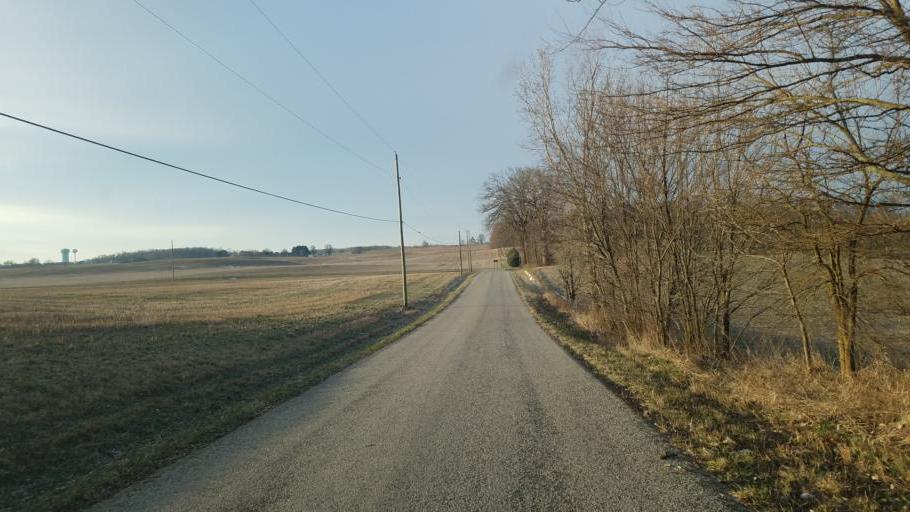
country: US
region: Ohio
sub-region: Knox County
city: Centerburg
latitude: 40.4111
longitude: -82.7209
